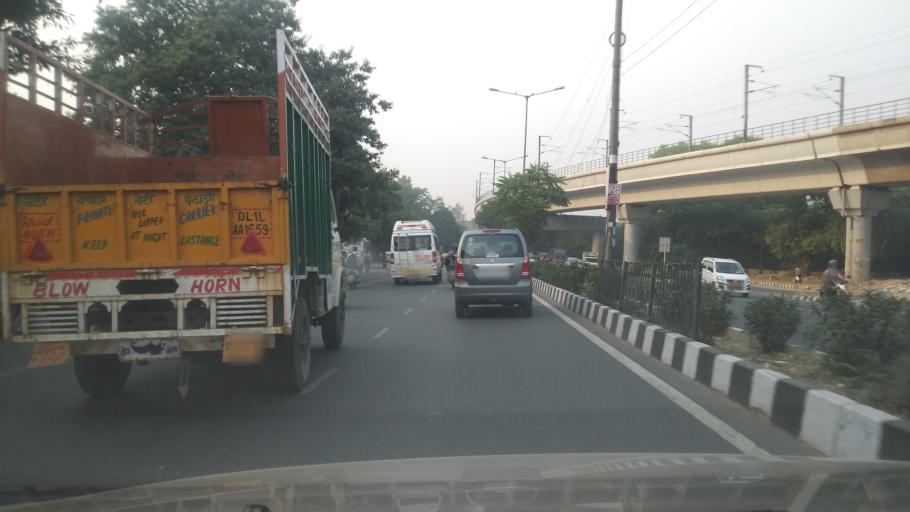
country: IN
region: Uttar Pradesh
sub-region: Gautam Buddha Nagar
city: Noida
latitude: 28.5404
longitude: 77.2659
